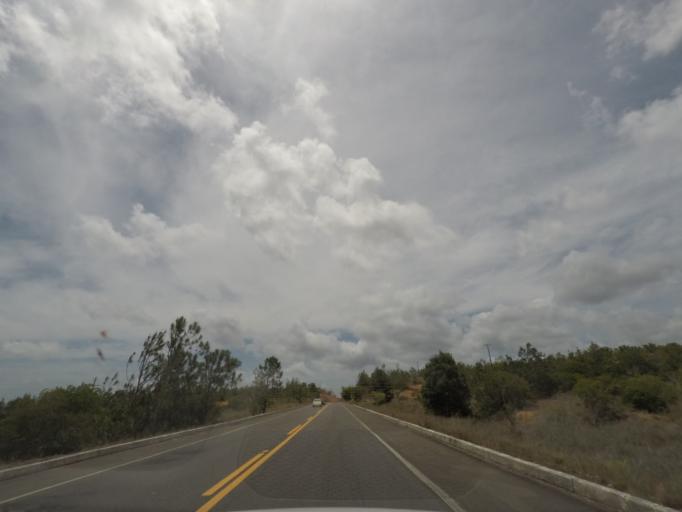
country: BR
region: Bahia
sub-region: Conde
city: Conde
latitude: -11.8783
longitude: -37.6443
